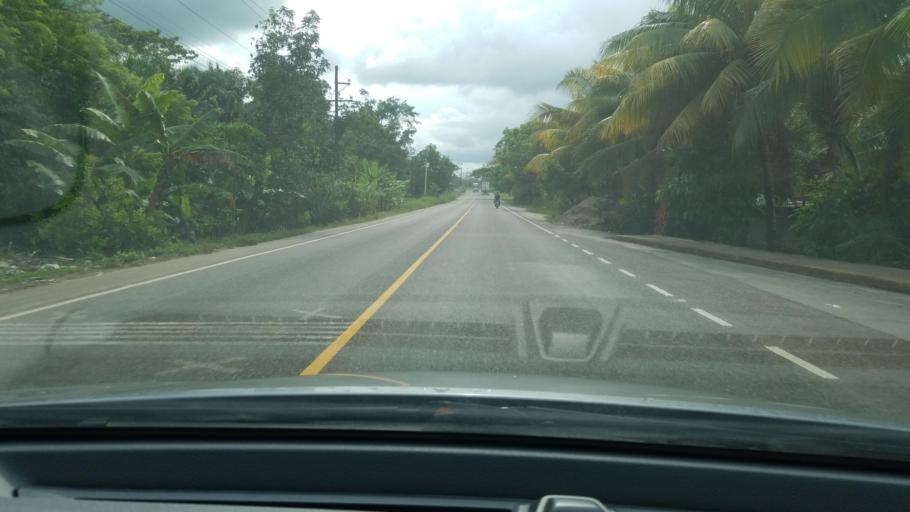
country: HN
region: Cortes
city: Potrerillos
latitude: 15.5942
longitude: -88.3113
